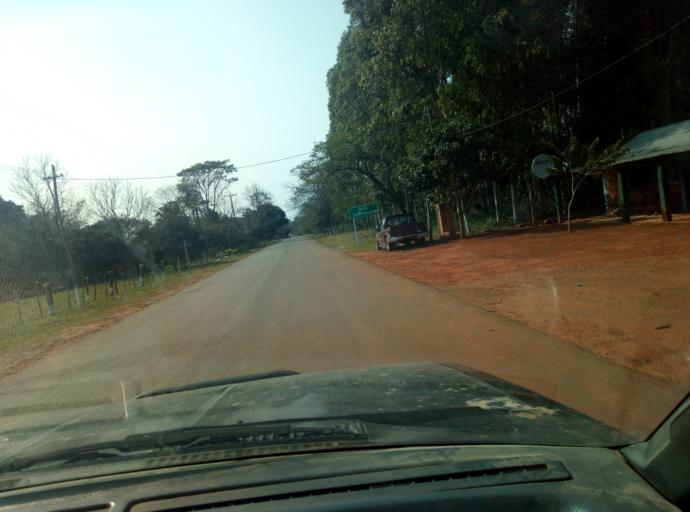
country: PY
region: Caaguazu
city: Carayao
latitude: -25.2101
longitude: -56.3062
